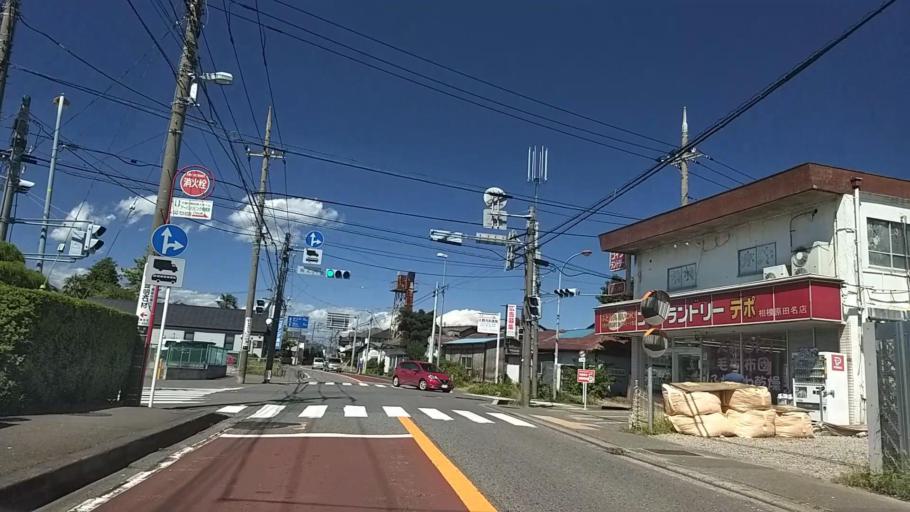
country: JP
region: Kanagawa
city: Zama
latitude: 35.5522
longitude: 139.3336
